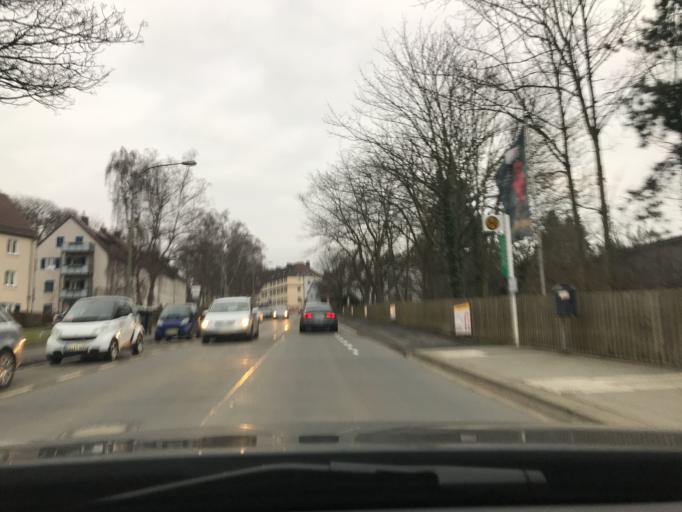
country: DE
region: Hesse
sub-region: Regierungsbezirk Kassel
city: Kassel
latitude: 51.3311
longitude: 9.5032
